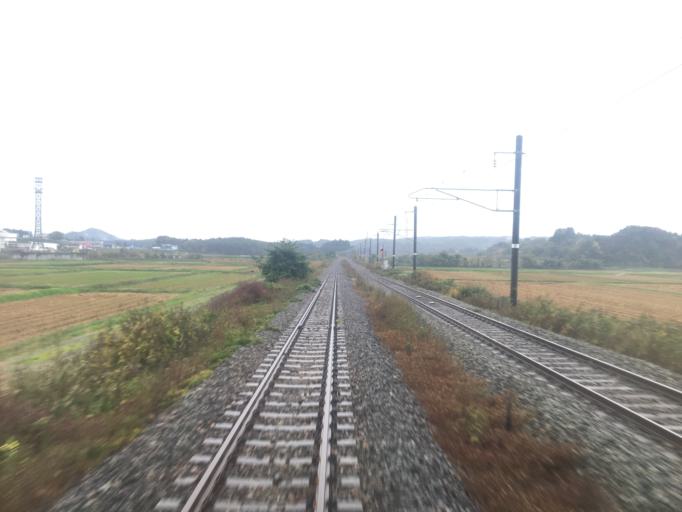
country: JP
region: Yamagata
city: Shinjo
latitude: 38.7417
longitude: 140.3077
